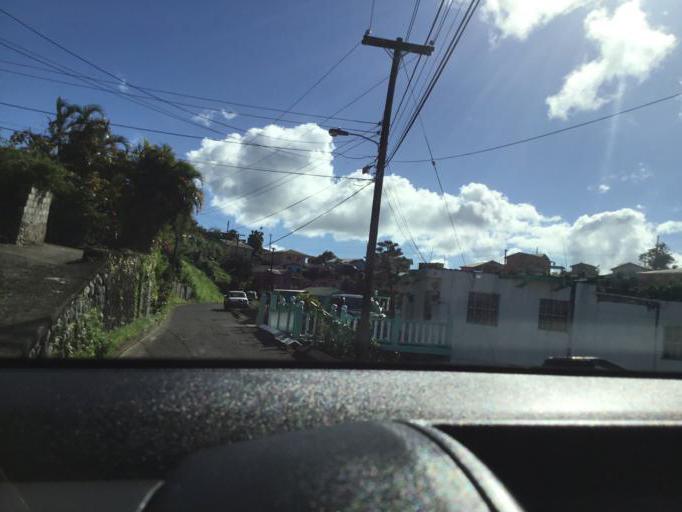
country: VC
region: Saint David
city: Chateaubelair
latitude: 13.2705
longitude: -61.2394
